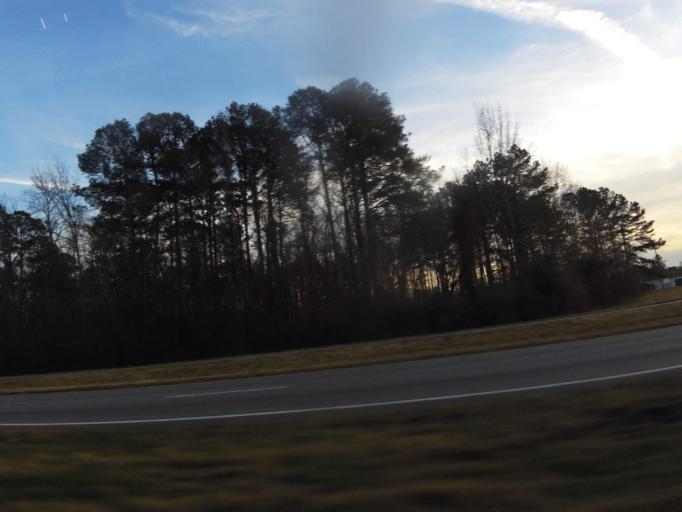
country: US
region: Virginia
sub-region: Southampton County
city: Courtland
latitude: 36.6829
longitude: -77.0032
